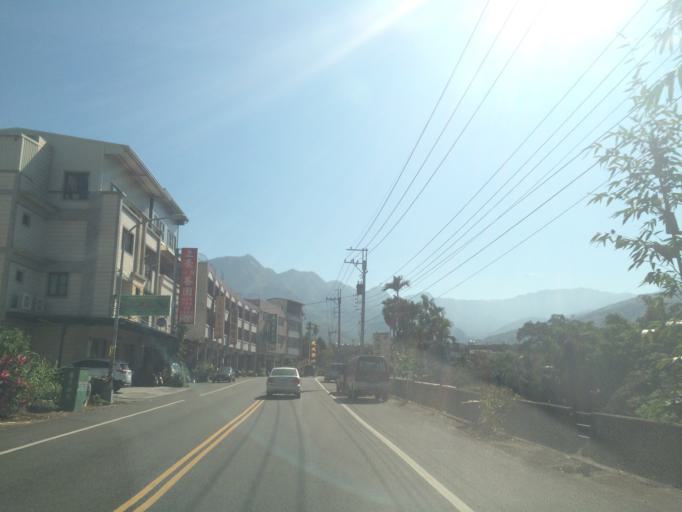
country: TW
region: Taiwan
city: Lugu
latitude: 23.7390
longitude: 120.7591
